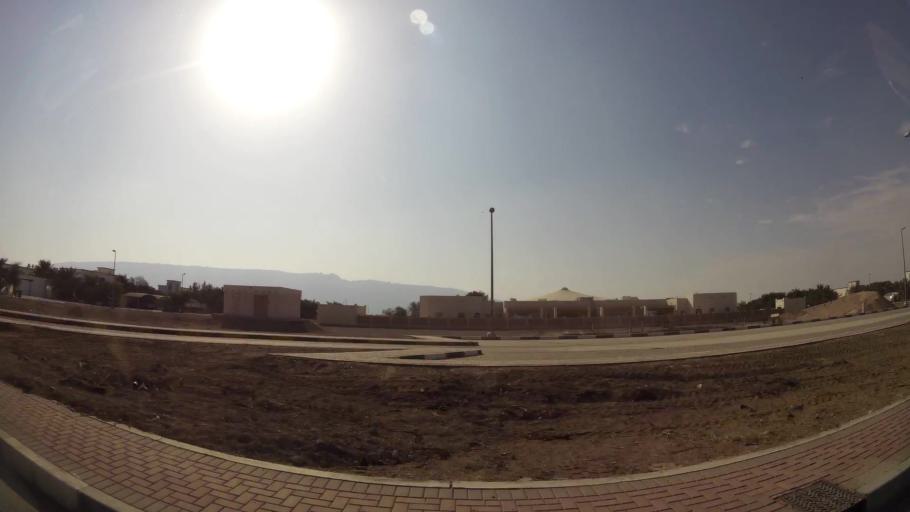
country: AE
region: Abu Dhabi
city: Al Ain
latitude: 24.0847
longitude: 55.8628
